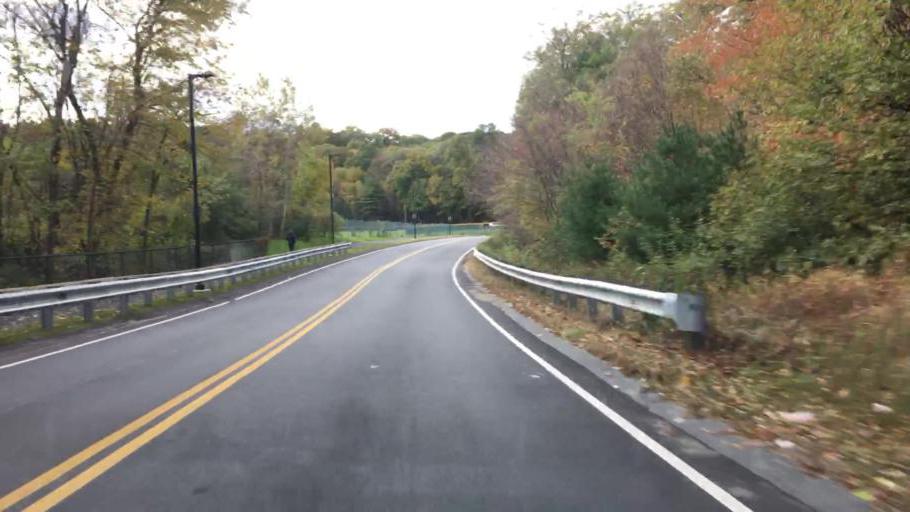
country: US
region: Massachusetts
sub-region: Middlesex County
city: Ashland
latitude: 42.2539
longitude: -71.4735
